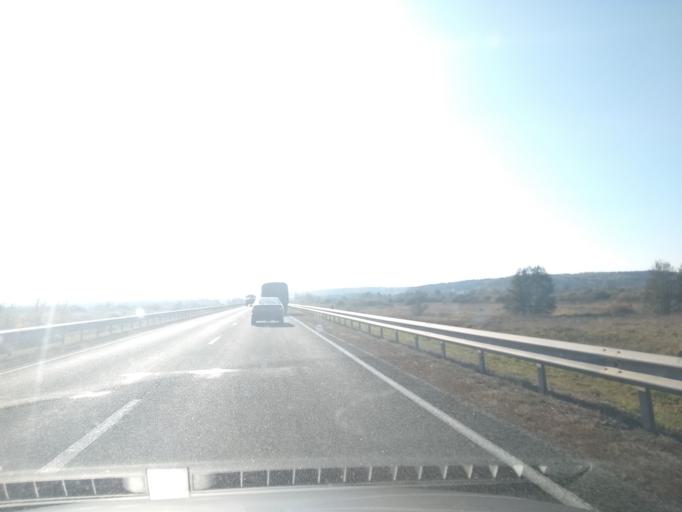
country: BY
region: Grodnenskaya
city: Zhyrovichy
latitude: 53.0532
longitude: 25.3780
